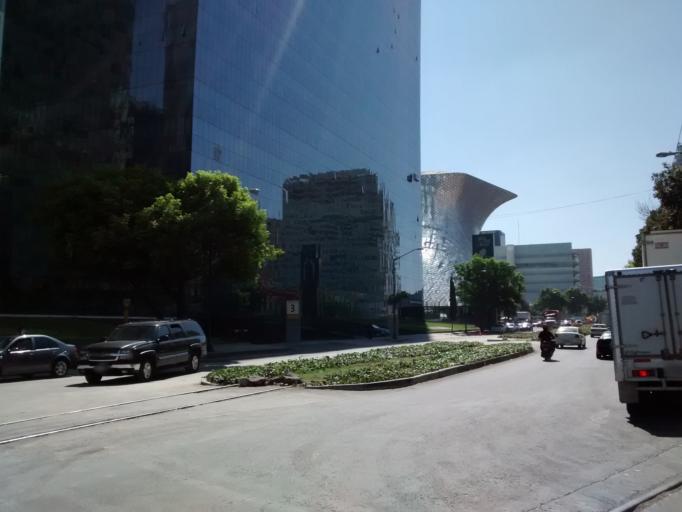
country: MX
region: Mexico City
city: Miguel Hidalgo
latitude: 19.4426
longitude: -99.2051
